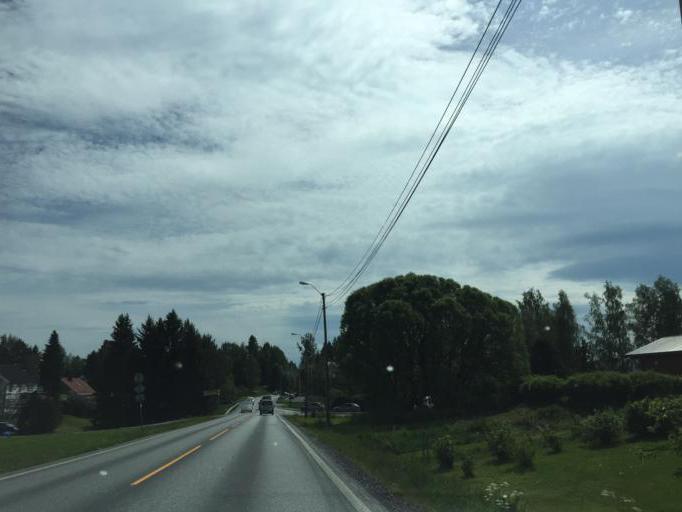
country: NO
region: Akershus
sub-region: Nes
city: Arnes
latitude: 60.1275
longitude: 11.4480
